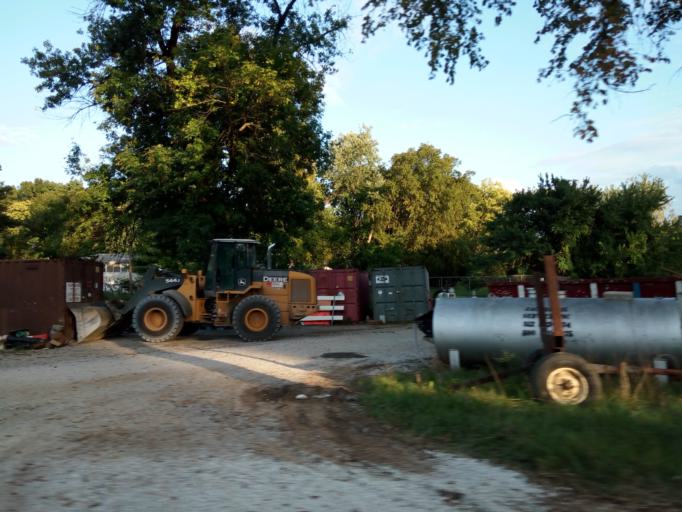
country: US
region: Kentucky
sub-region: Jefferson County
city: Audubon Park
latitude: 38.2055
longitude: -85.7194
